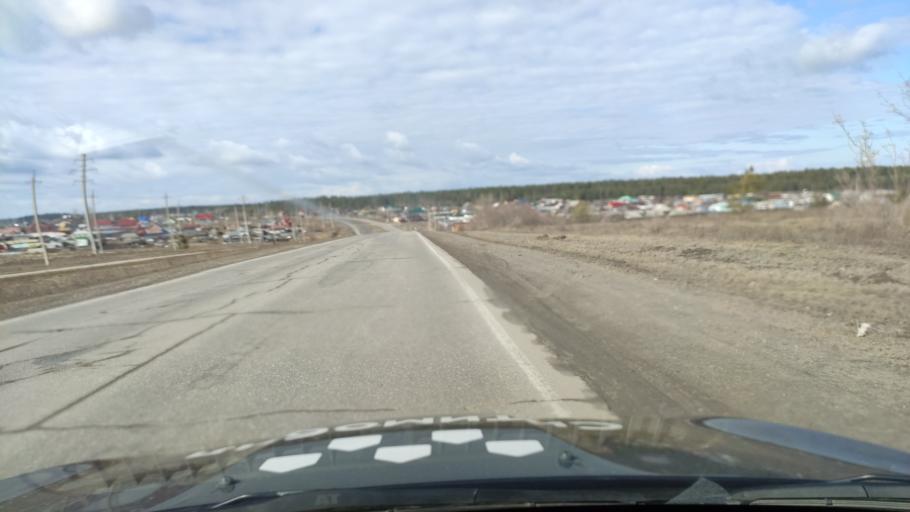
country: RU
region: Samara
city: Povolzhskiy
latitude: 53.5878
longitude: 49.7397
